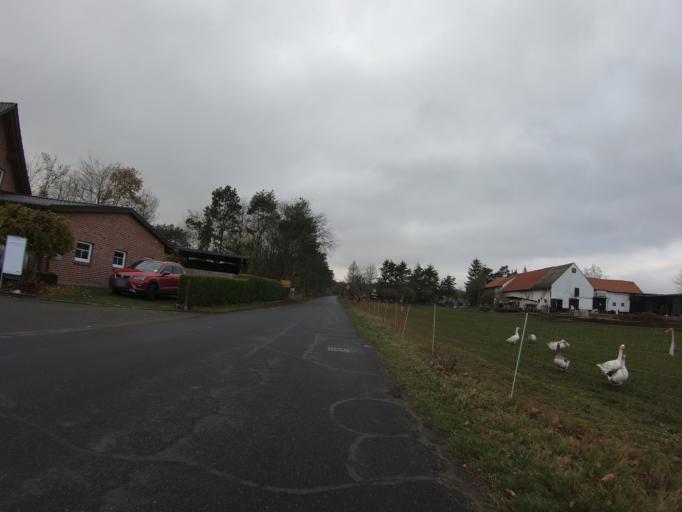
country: DE
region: Lower Saxony
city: Wagenhoff
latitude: 52.5554
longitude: 10.5195
